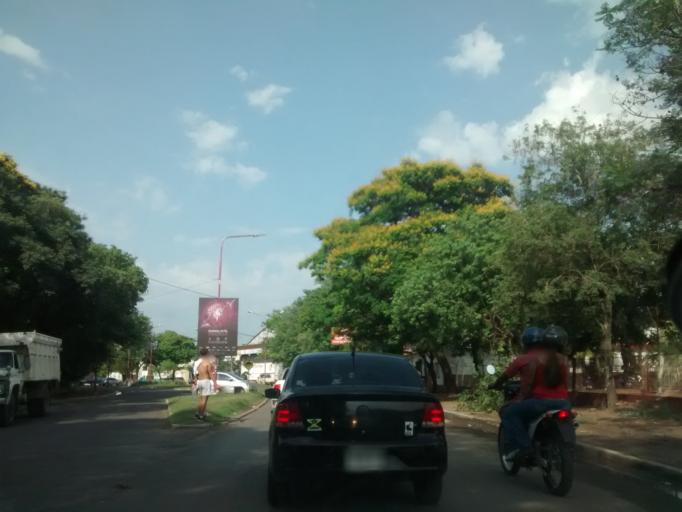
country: AR
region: Chaco
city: Resistencia
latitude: -27.4364
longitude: -58.9836
